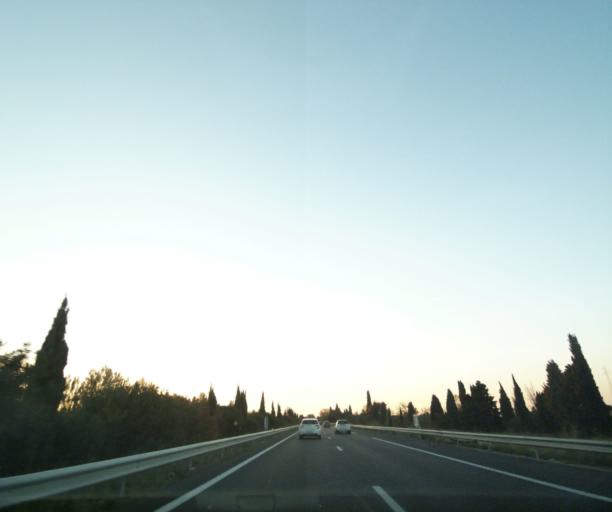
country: FR
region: Provence-Alpes-Cote d'Azur
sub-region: Departement des Bouches-du-Rhone
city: Mouries
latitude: 43.6392
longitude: 4.8812
